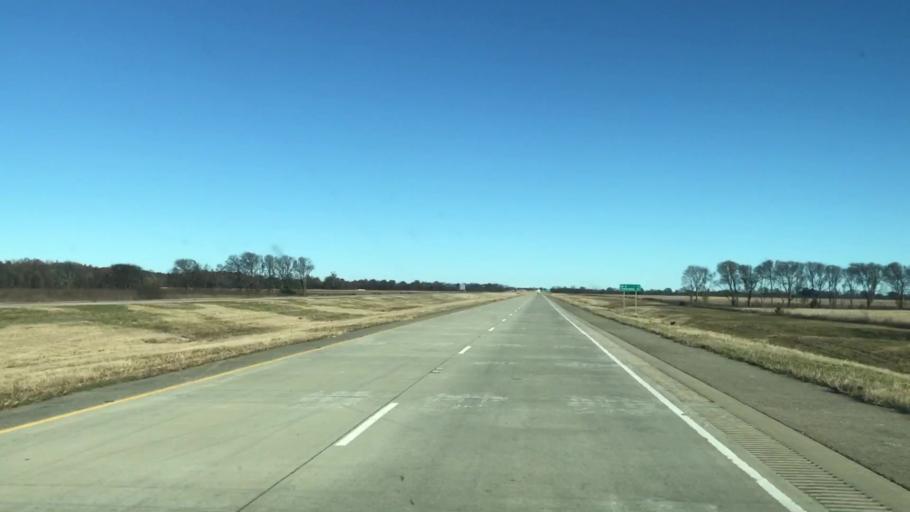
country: US
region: Louisiana
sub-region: Caddo Parish
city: Vivian
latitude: 32.8655
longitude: -93.8601
